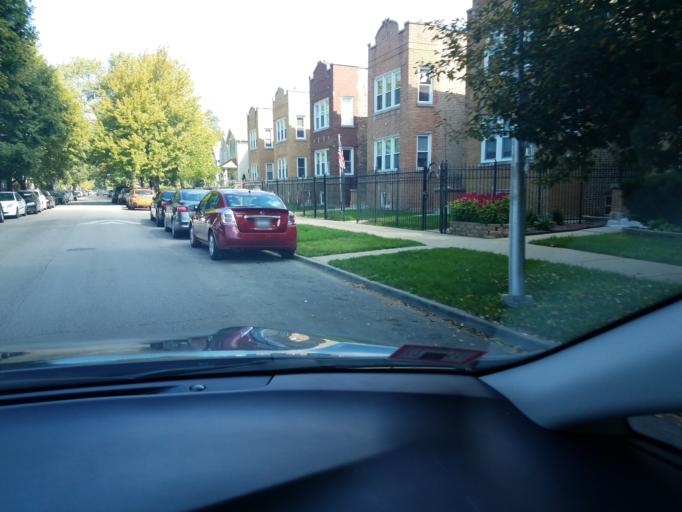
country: US
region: Illinois
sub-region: Cook County
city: Lincolnwood
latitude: 41.9511
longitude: -87.7031
